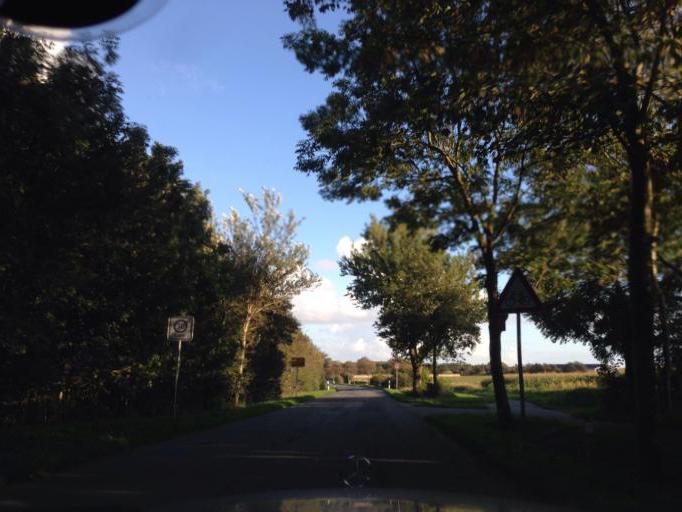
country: DE
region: Schleswig-Holstein
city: Borgsum
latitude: 54.6970
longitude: 8.4637
